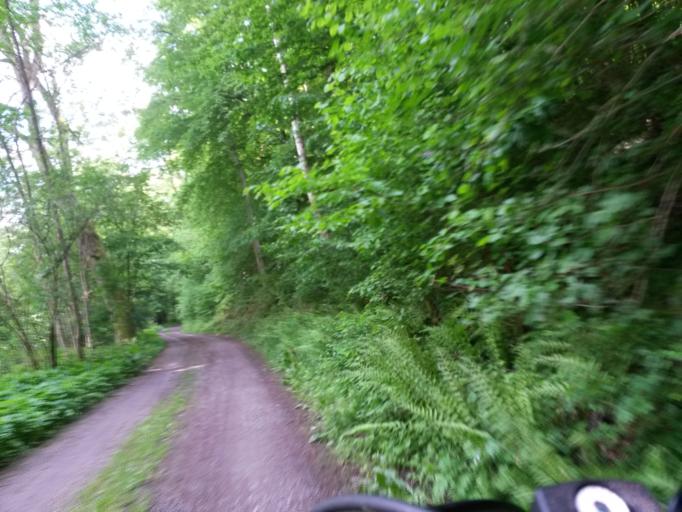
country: DE
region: Bavaria
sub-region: Regierungsbezirk Unterfranken
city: Ramsthal
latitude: 50.1688
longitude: 10.0537
